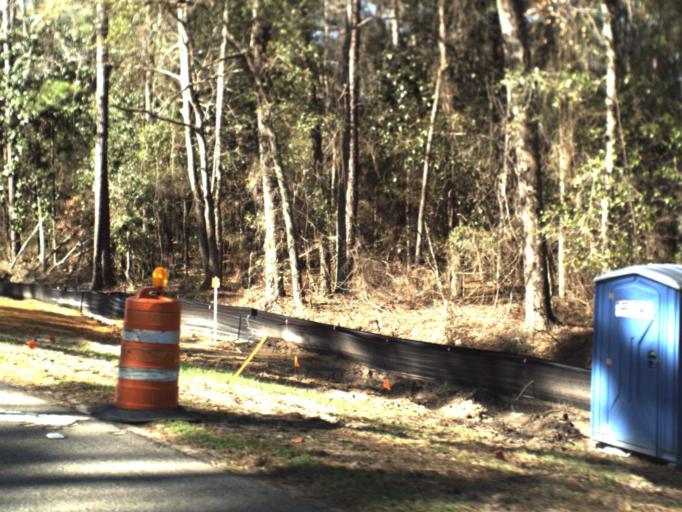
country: US
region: Florida
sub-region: Calhoun County
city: Blountstown
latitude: 30.4284
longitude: -85.1678
